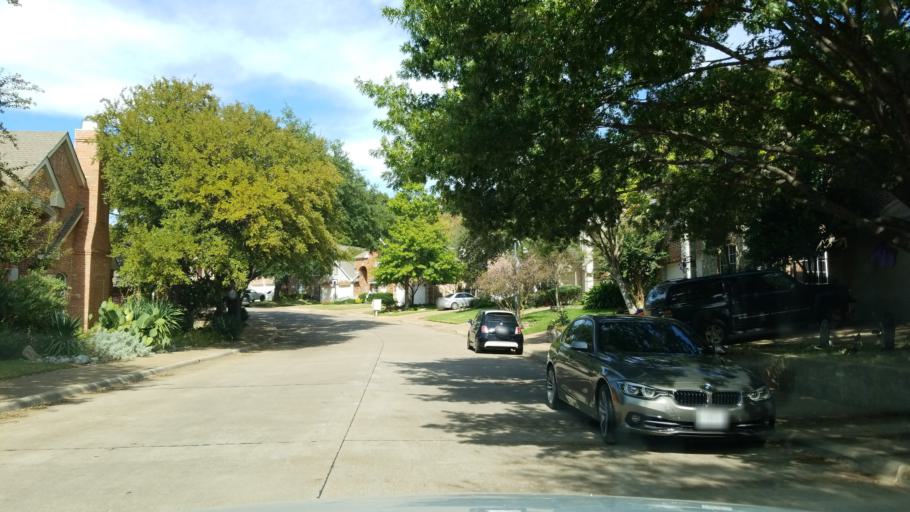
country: US
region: Texas
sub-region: Dallas County
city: Highland Park
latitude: 32.8120
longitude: -96.7236
